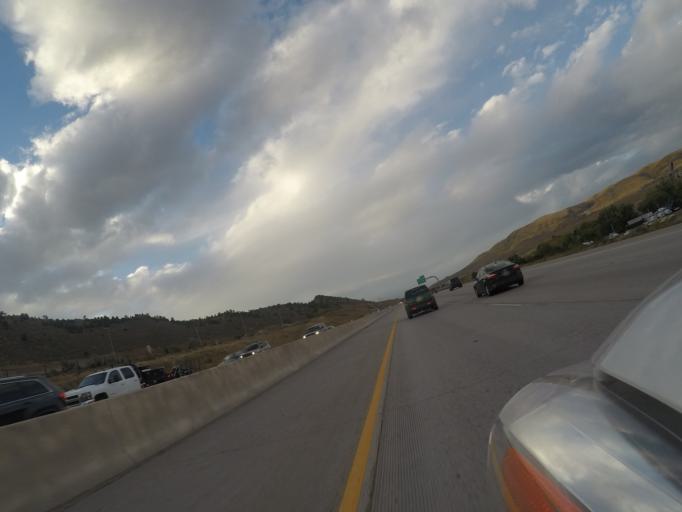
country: US
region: Colorado
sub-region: Jefferson County
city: West Pleasant View
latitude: 39.6649
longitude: -105.1861
